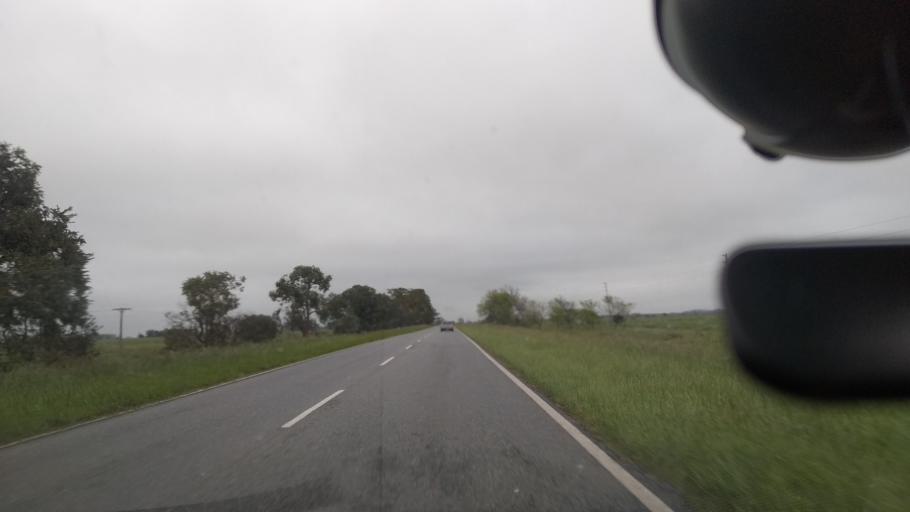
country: AR
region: Buenos Aires
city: Veronica
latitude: -35.3009
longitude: -57.5168
